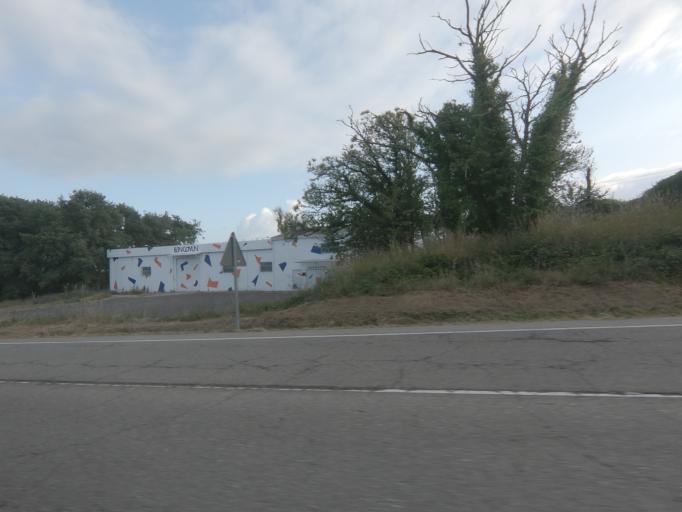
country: ES
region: Galicia
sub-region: Provincia de Ourense
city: Taboadela
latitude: 42.2136
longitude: -7.8230
